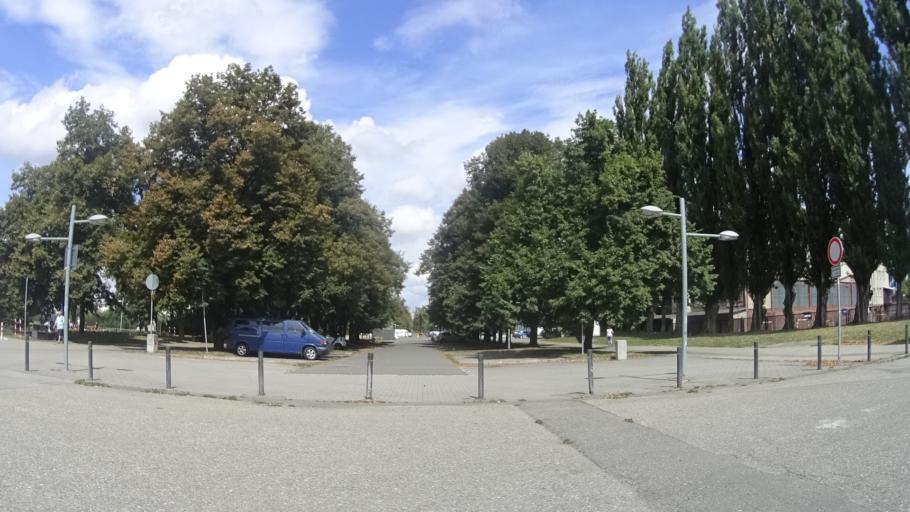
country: CZ
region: Olomoucky
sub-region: Okres Olomouc
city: Olomouc
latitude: 49.5987
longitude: 17.2464
